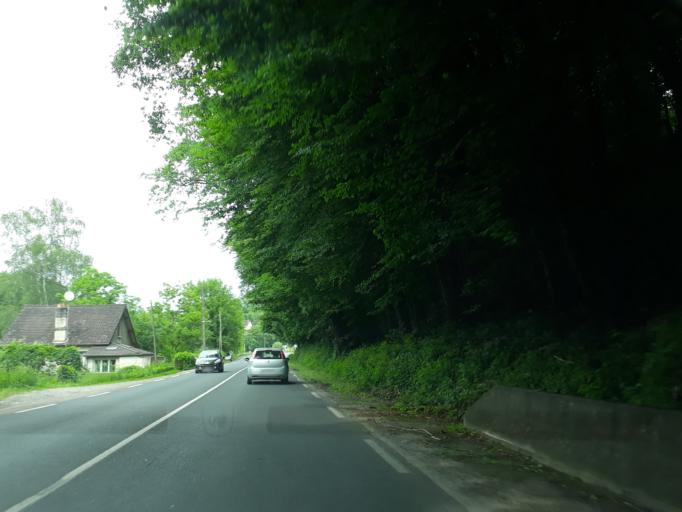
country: FR
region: Limousin
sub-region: Departement de la Correze
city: Saint-Pantaleon-de-Larche
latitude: 45.1353
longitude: 1.4456
